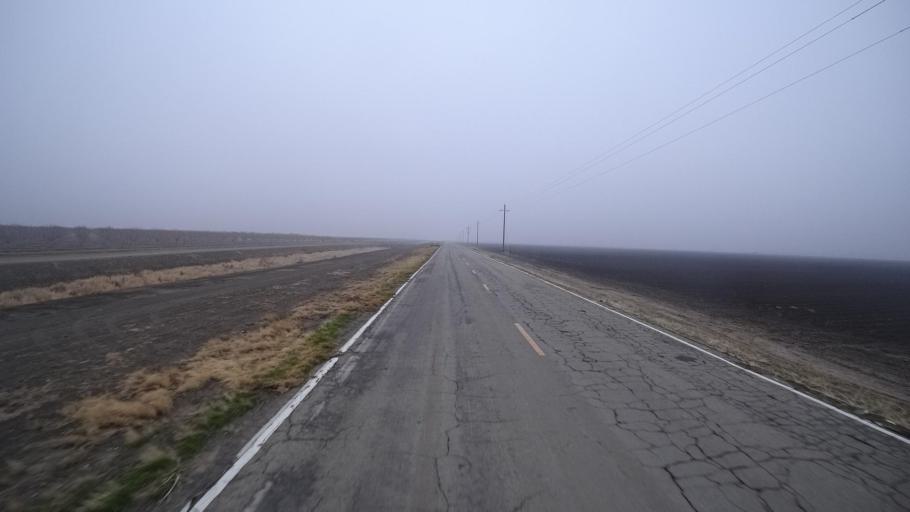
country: US
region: California
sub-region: Kern County
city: Lost Hills
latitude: 35.5445
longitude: -119.6187
